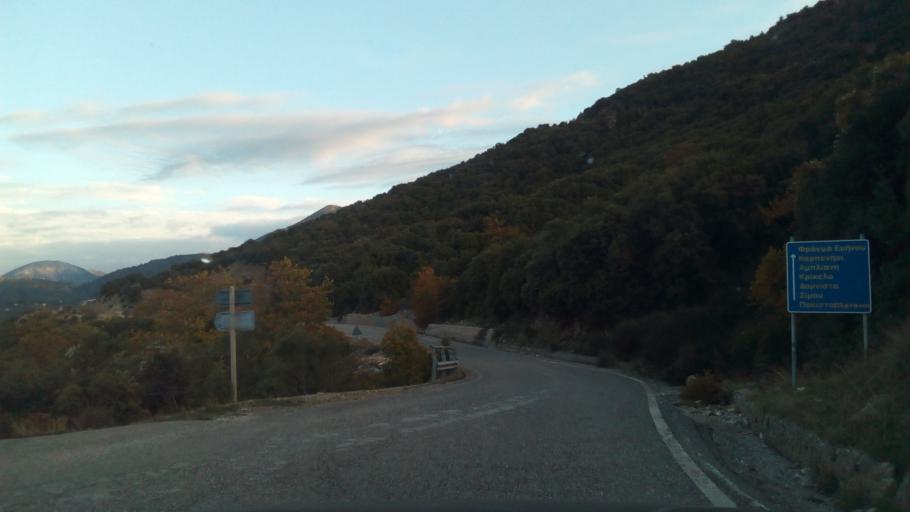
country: GR
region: West Greece
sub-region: Nomos Aitolias kai Akarnanias
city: Nafpaktos
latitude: 38.5055
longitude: 21.8356
